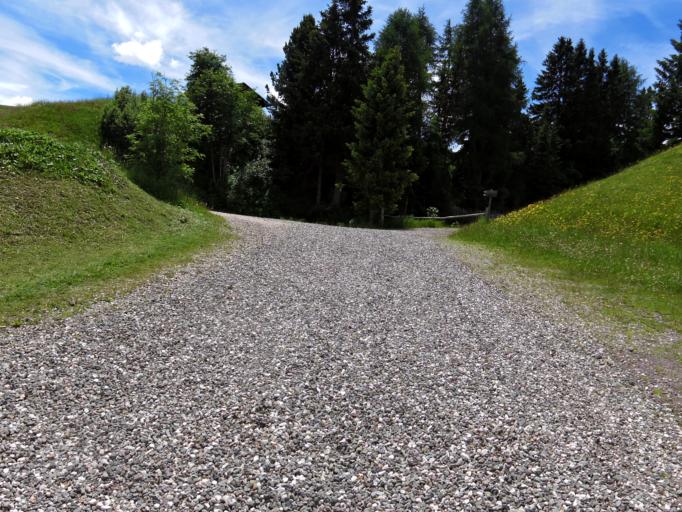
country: IT
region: Trentino-Alto Adige
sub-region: Bolzano
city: Ortisei
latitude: 46.5394
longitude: 11.6445
